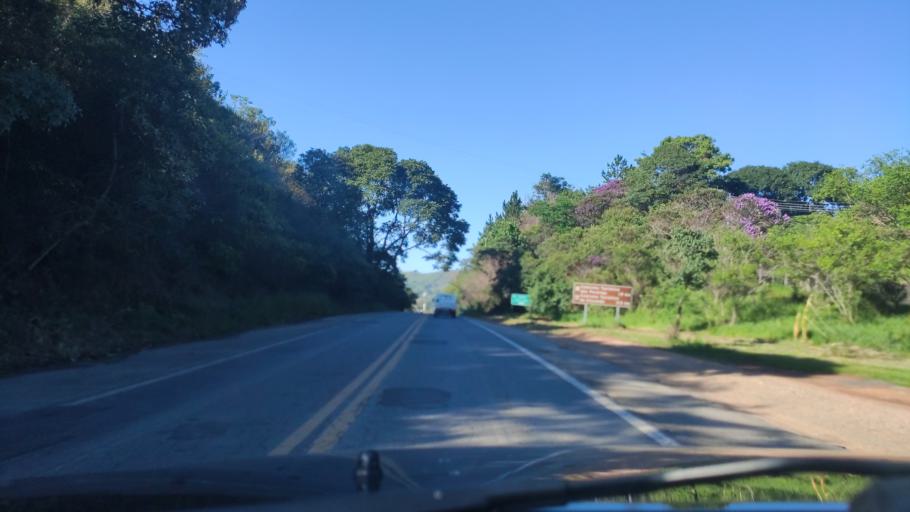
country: BR
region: Sao Paulo
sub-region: Socorro
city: Socorro
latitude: -22.6005
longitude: -46.5213
